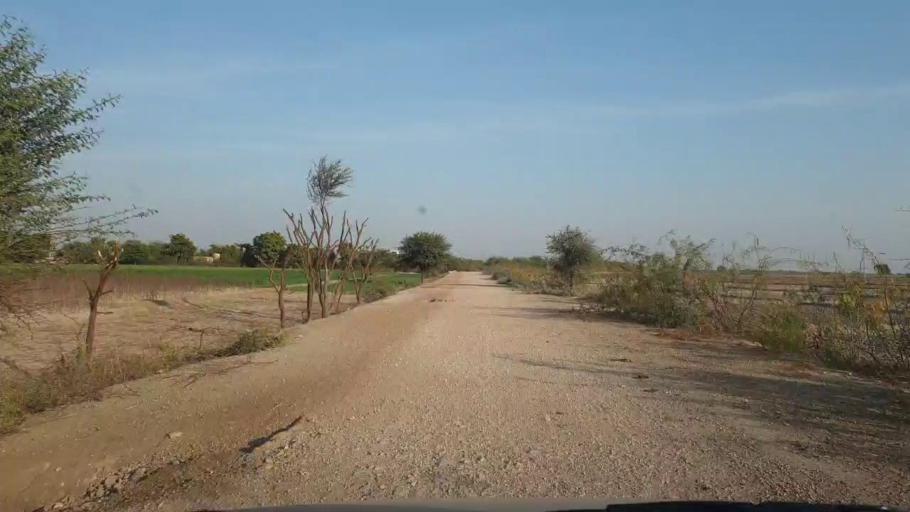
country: PK
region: Sindh
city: Chambar
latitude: 25.2386
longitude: 68.8022
